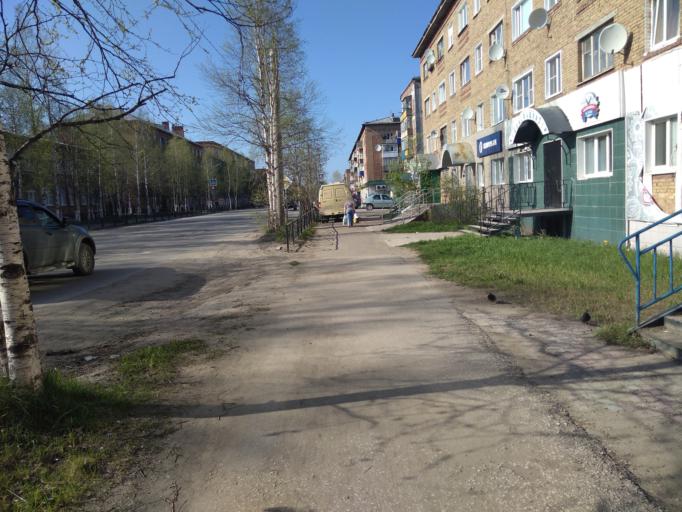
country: RU
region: Komi Republic
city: Pechora
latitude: 65.1232
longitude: 57.1543
